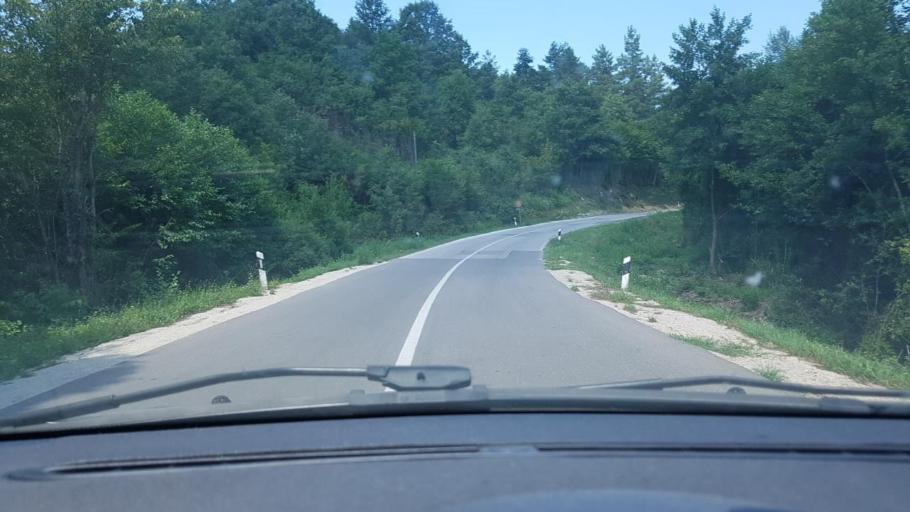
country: BA
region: Federation of Bosnia and Herzegovina
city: Orasac
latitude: 44.6036
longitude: 16.0704
